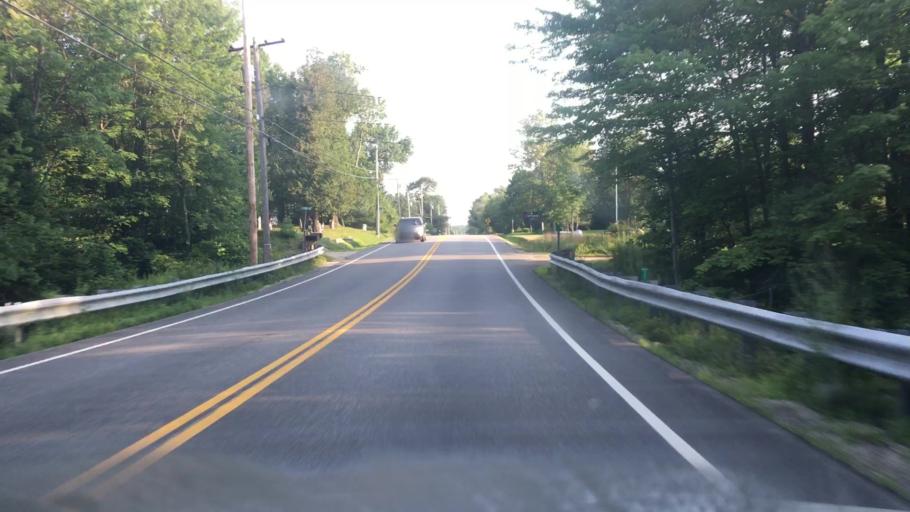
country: US
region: Maine
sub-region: Cumberland County
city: Freeport
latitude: 43.9083
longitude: -70.0920
